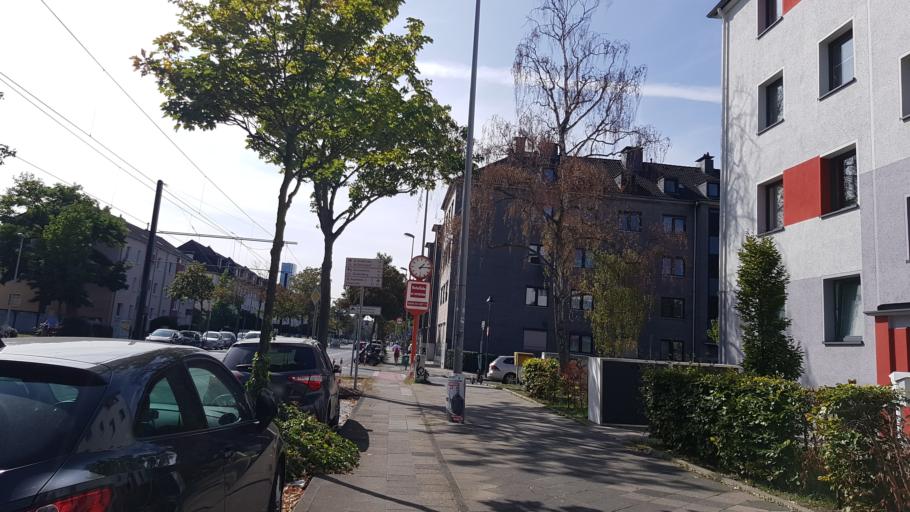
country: DE
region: North Rhine-Westphalia
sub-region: Regierungsbezirk Dusseldorf
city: Dusseldorf
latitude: 51.2602
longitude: 6.8084
